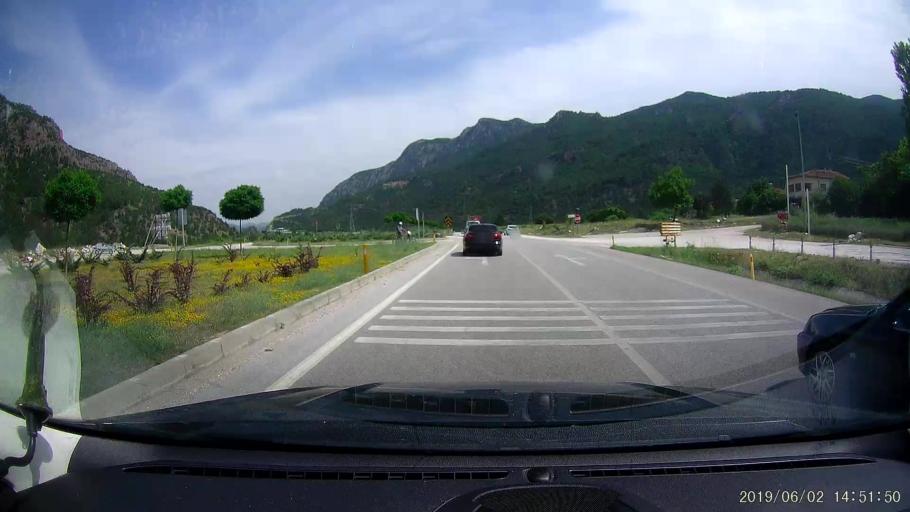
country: TR
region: Corum
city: Hacihamza
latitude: 41.0543
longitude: 34.5450
